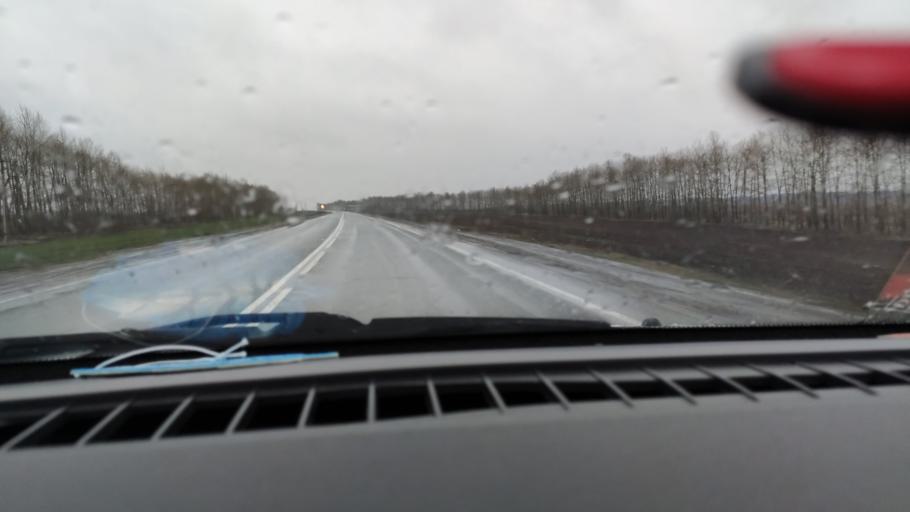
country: RU
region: Tatarstan
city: Mendeleyevsk
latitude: 55.9220
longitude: 52.2752
